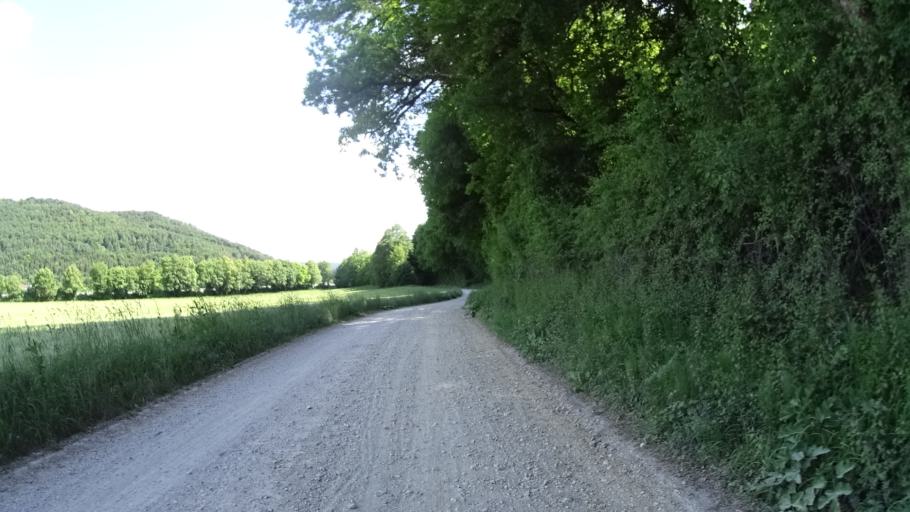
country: DE
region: Bavaria
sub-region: Regierungsbezirk Mittelfranken
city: Greding
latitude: 49.0165
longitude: 11.3559
